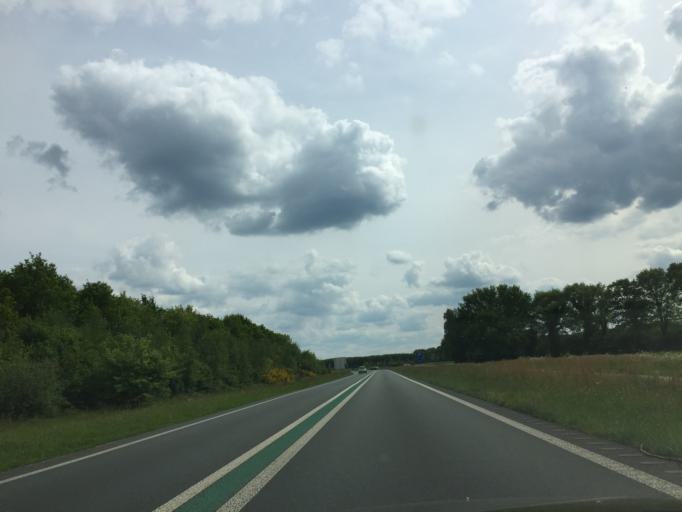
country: NL
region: Drenthe
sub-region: Gemeente Aa en Hunze
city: Anloo
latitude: 53.0056
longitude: 6.7506
